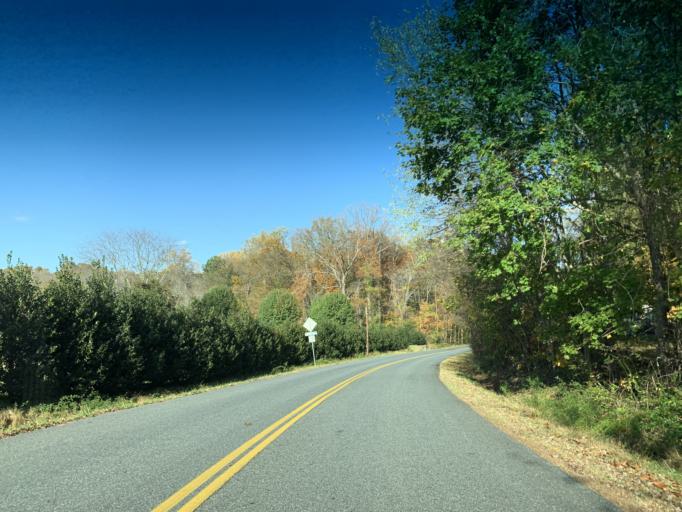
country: US
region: Maryland
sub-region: Harford County
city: Joppatowne
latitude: 39.4753
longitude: -76.3575
